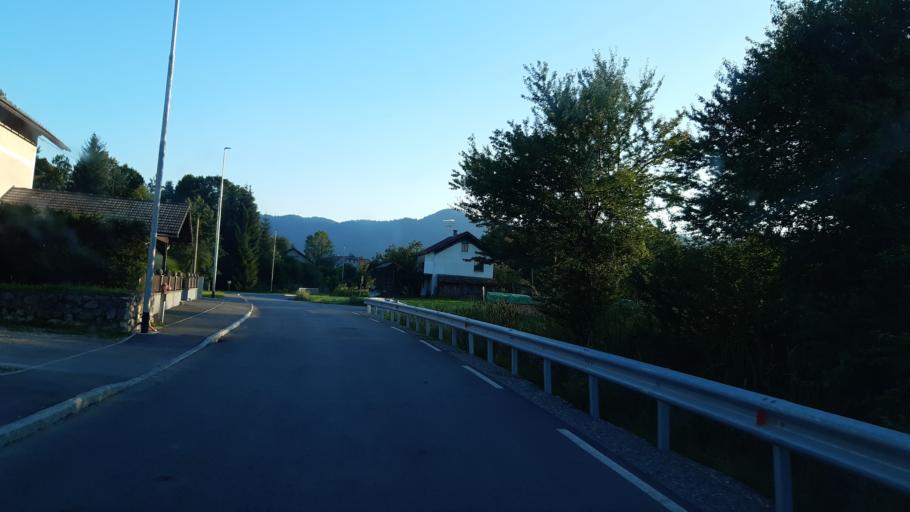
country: SI
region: Kocevje
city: Kocevje
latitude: 45.6558
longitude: 14.8824
